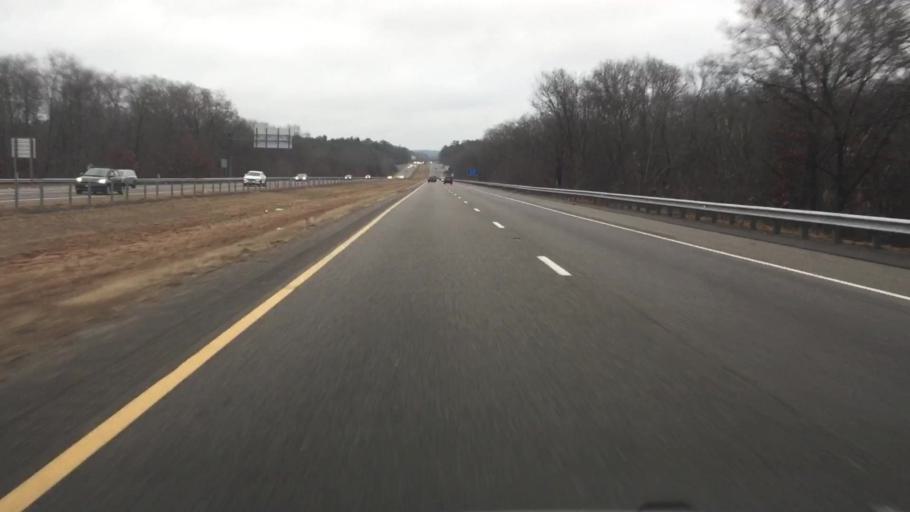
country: US
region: Massachusetts
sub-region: Plymouth County
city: Middleborough Center
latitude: 41.8814
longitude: -70.9187
